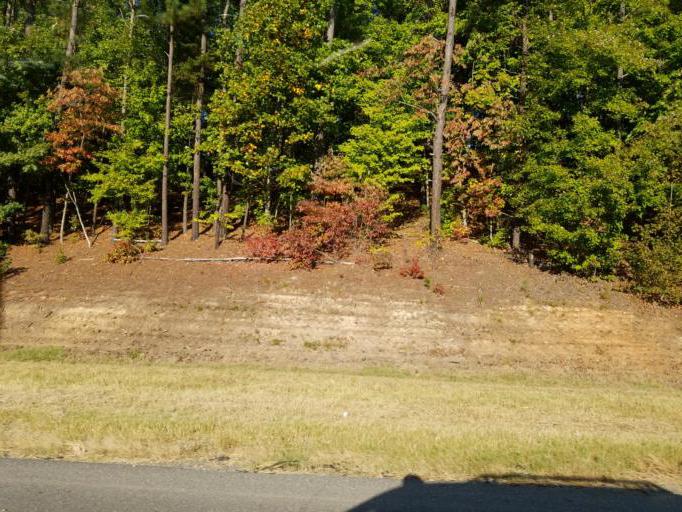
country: US
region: Georgia
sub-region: Bartow County
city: Emerson
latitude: 34.1568
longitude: -84.7508
